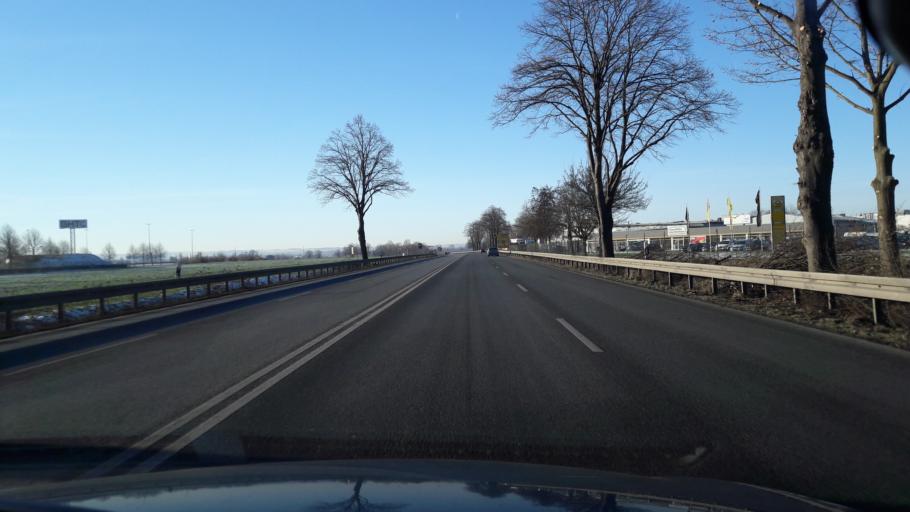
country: DE
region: North Rhine-Westphalia
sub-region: Regierungsbezirk Arnsberg
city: Lippstadt
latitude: 51.6531
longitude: 8.3482
